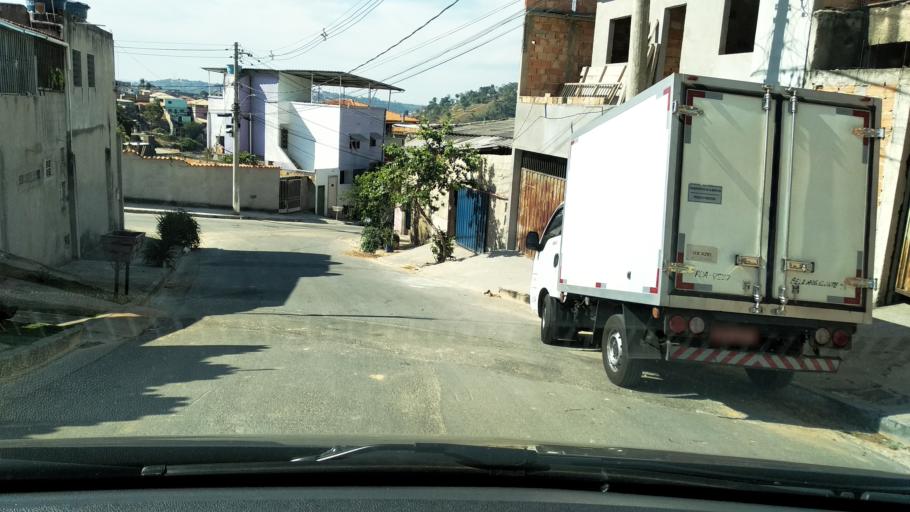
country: BR
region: Minas Gerais
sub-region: Belo Horizonte
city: Belo Horizonte
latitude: -19.8598
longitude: -43.8774
